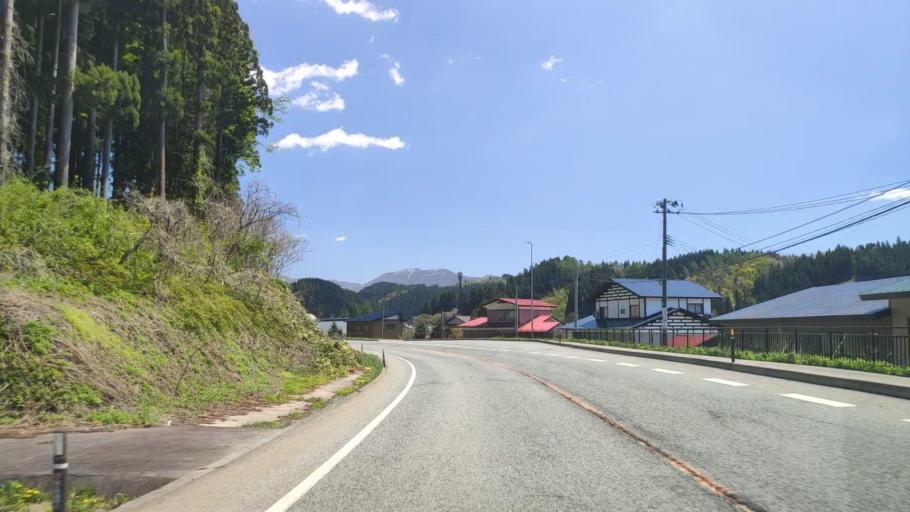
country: JP
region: Yamagata
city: Shinjo
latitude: 38.8894
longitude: 140.3260
